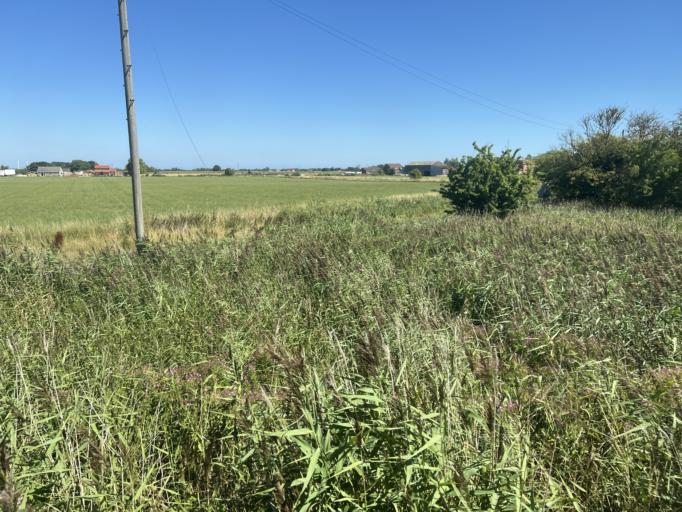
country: GB
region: England
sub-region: Lincolnshire
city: Wainfleet All Saints
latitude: 53.1089
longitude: 0.2266
